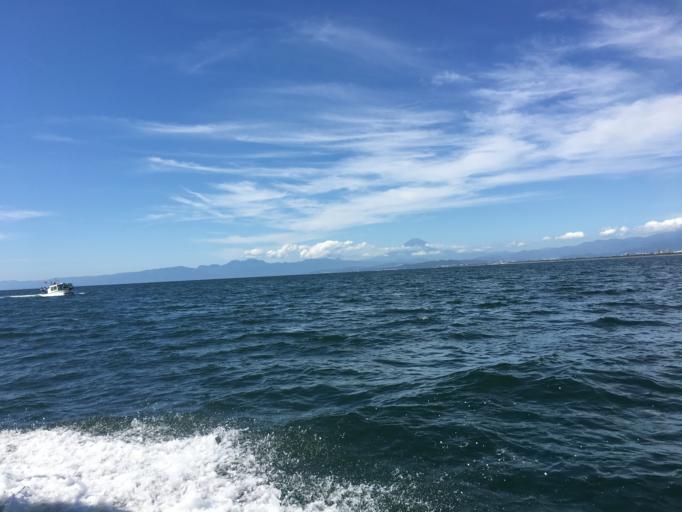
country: JP
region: Kanagawa
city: Fujisawa
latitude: 35.3026
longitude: 139.4769
